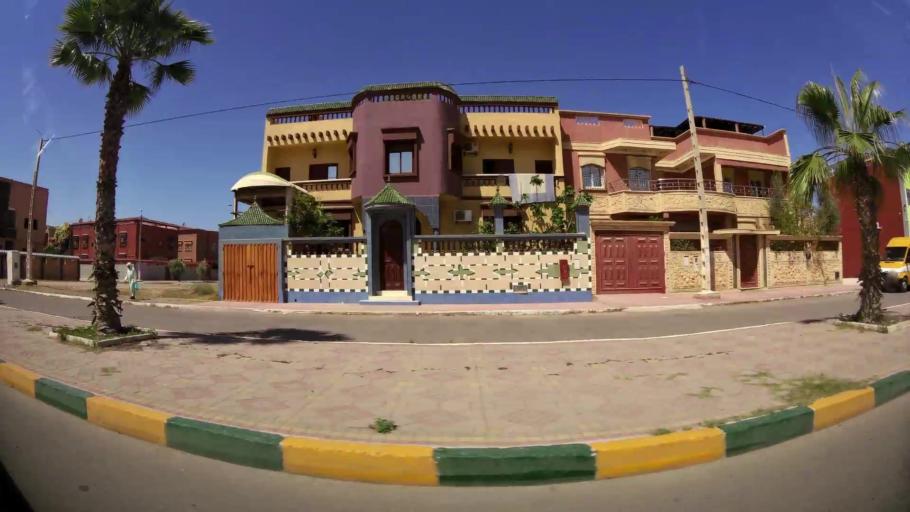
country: MA
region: Souss-Massa-Draa
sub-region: Inezgane-Ait Mellou
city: Inezgane
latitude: 30.3228
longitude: -9.5035
